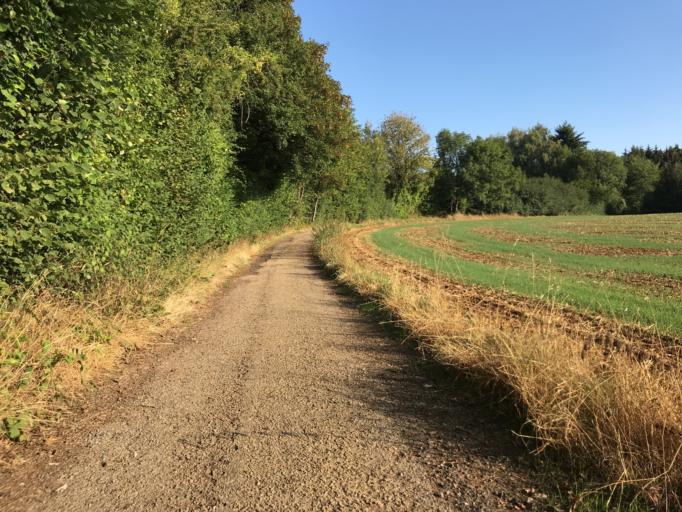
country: LU
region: Luxembourg
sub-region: Canton d'Esch-sur-Alzette
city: Niedercorn
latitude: 49.5338
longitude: 5.8729
